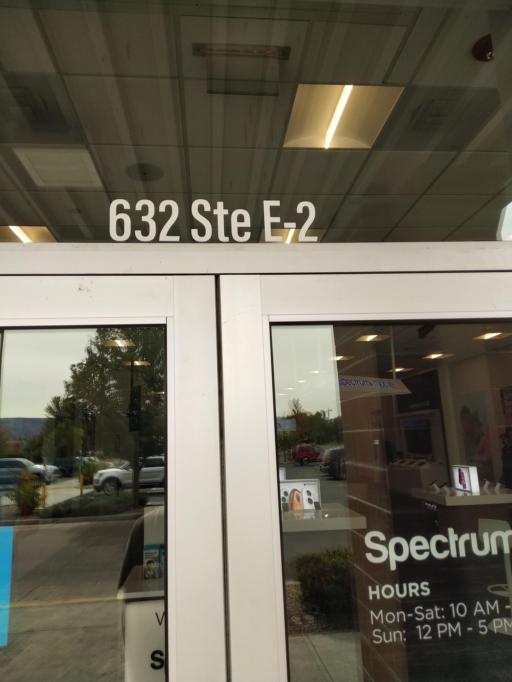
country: US
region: Colorado
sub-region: Mesa County
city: Redlands
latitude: 39.0960
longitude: -108.6041
